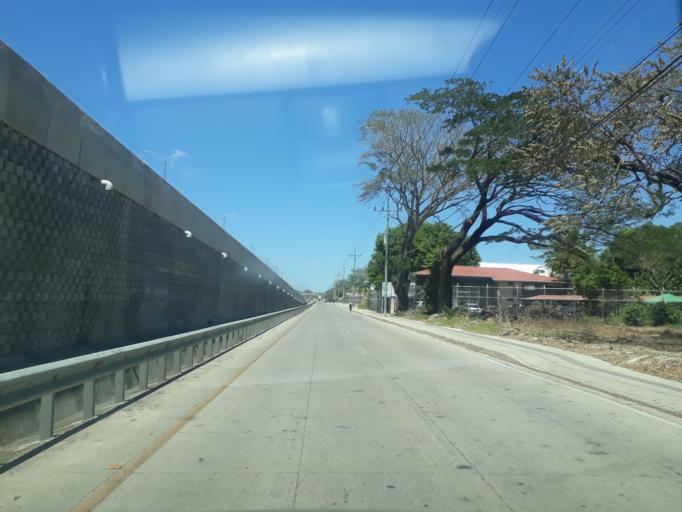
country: CR
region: Guanacaste
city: Liberia
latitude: 10.6318
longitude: -85.4468
